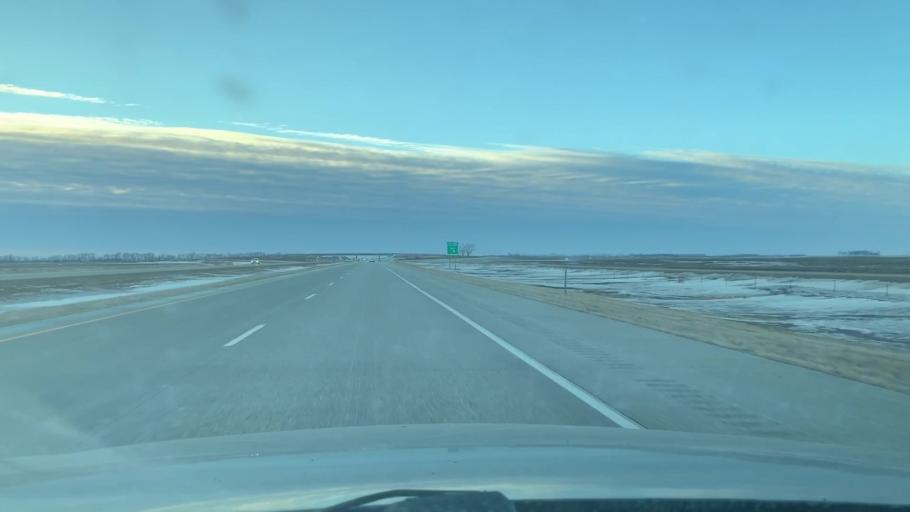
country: US
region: North Dakota
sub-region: Cass County
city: Casselton
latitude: 46.8758
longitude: -97.4835
